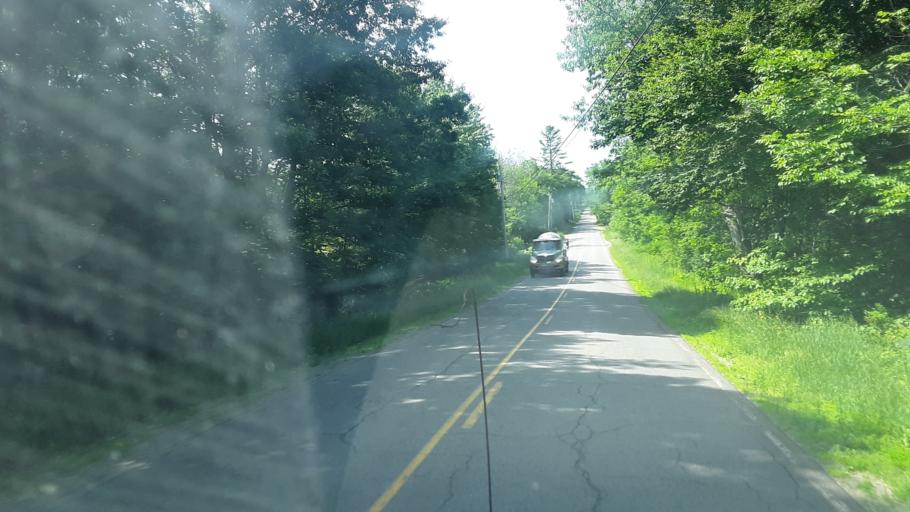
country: US
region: Maine
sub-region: Waldo County
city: Swanville
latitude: 44.5786
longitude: -68.9482
